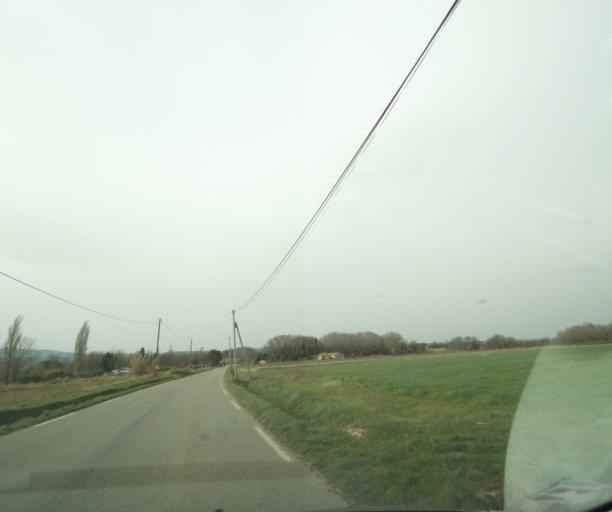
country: FR
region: Provence-Alpes-Cote d'Azur
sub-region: Departement des Bouches-du-Rhone
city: Trets
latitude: 43.4641
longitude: 5.7027
